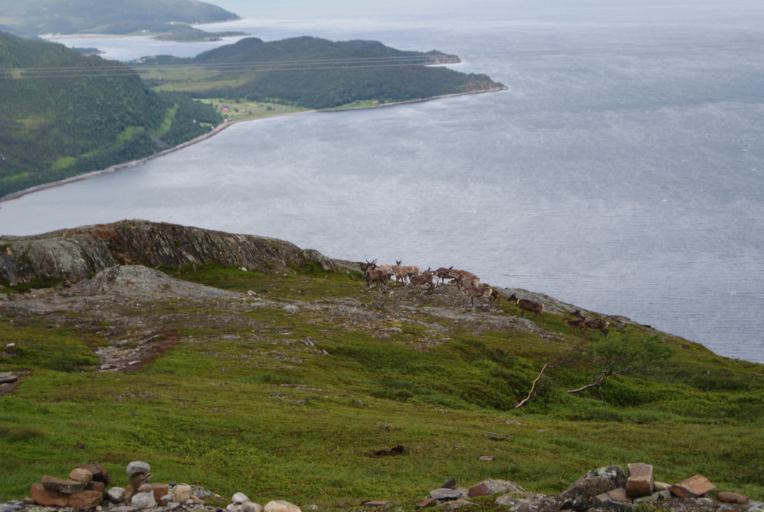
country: NO
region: Troms
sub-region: Kvaenangen
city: Burfjord
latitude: 69.8998
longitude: 21.5972
